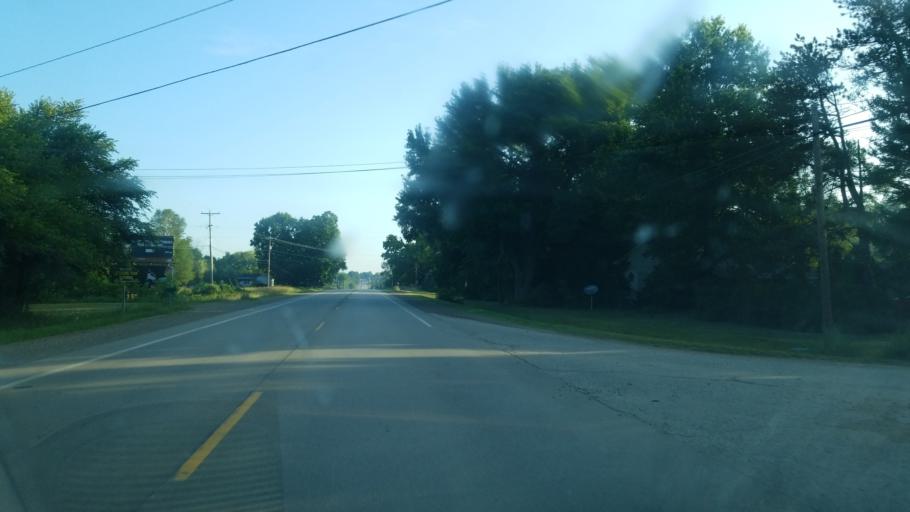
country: US
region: Michigan
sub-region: Montcalm County
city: Stanton
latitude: 43.2789
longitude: -85.0738
